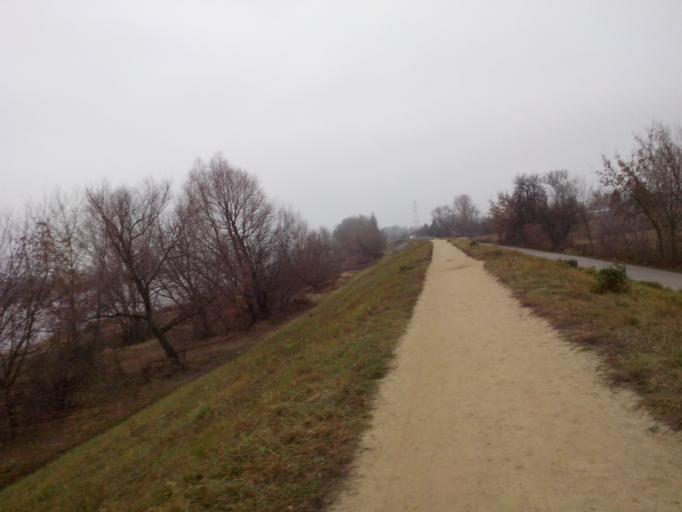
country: PL
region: Masovian Voivodeship
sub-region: Powiat legionowski
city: Jablonna
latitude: 52.3408
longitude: 20.9289
